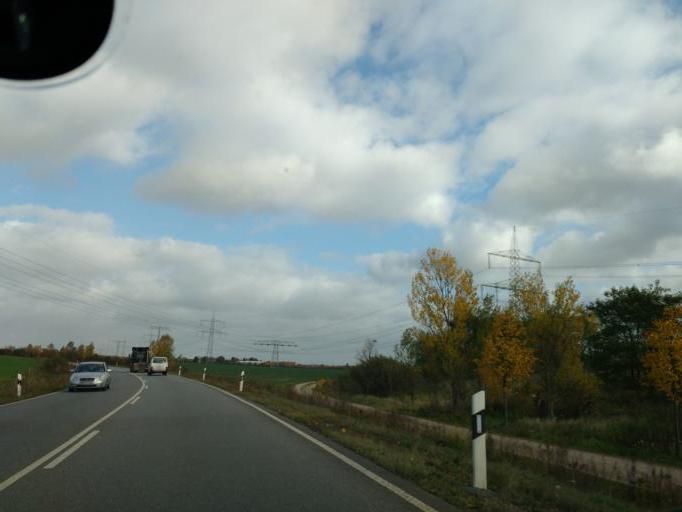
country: DE
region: Brandenburg
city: Altlandsberg
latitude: 52.5450
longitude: 13.7253
